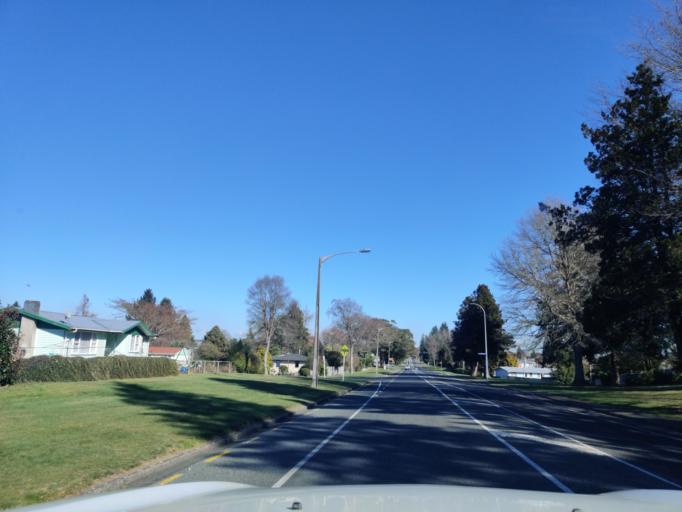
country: NZ
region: Waikato
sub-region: South Waikato District
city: Tokoroa
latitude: -38.2278
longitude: 175.8695
